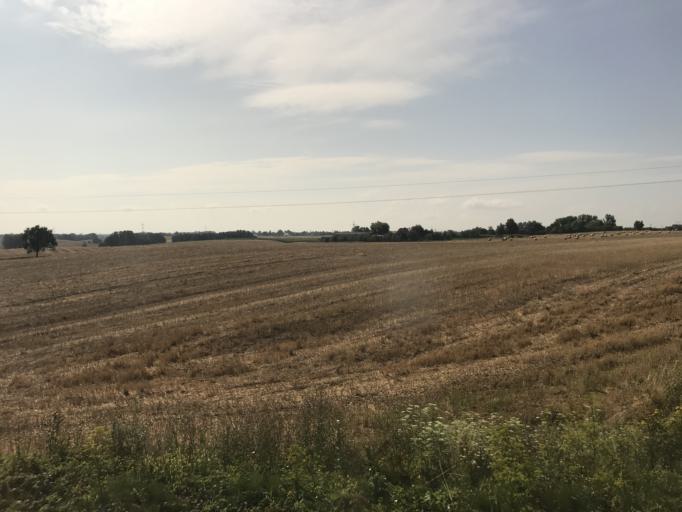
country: PL
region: Kujawsko-Pomorskie
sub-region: Powiat swiecki
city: Pruszcz
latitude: 53.3646
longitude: 18.2504
